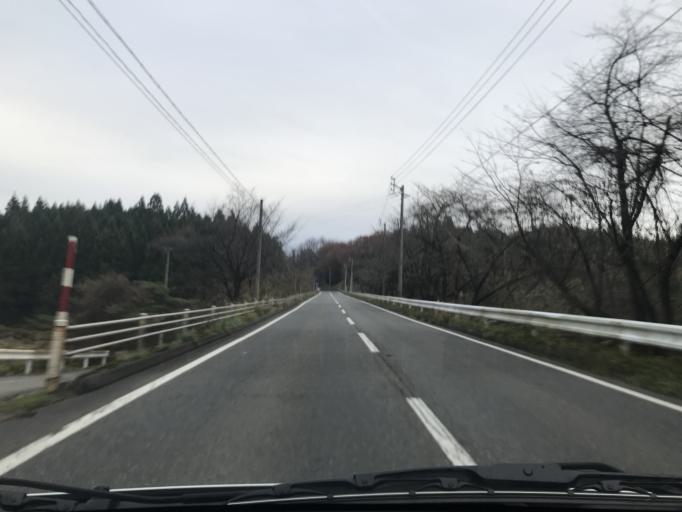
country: JP
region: Iwate
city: Kitakami
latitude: 39.2851
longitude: 141.2287
